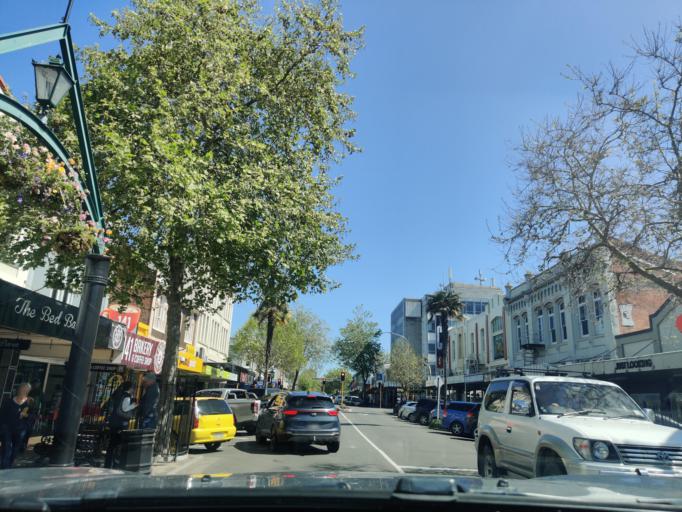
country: NZ
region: Manawatu-Wanganui
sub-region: Wanganui District
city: Wanganui
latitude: -39.9320
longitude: 175.0505
